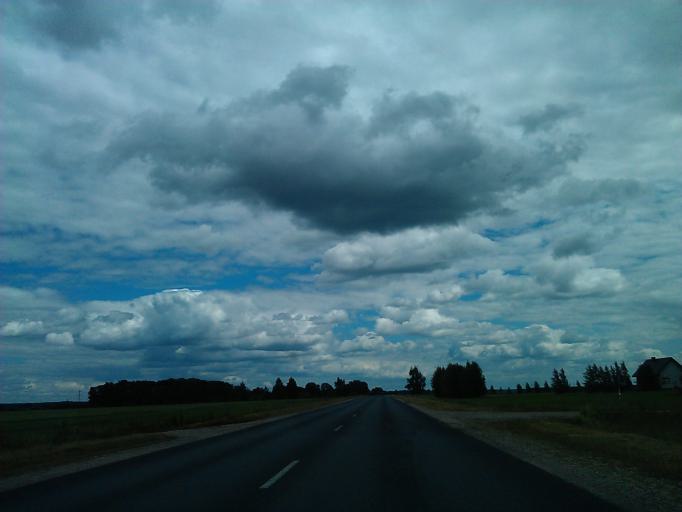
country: LV
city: Tervete
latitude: 56.6218
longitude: 23.4664
